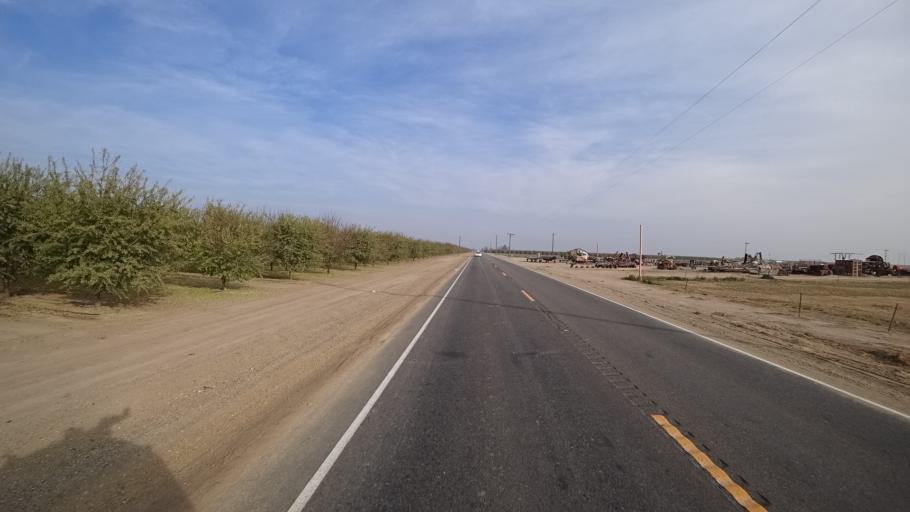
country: US
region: California
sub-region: Kern County
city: Rosedale
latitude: 35.2672
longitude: -119.1385
